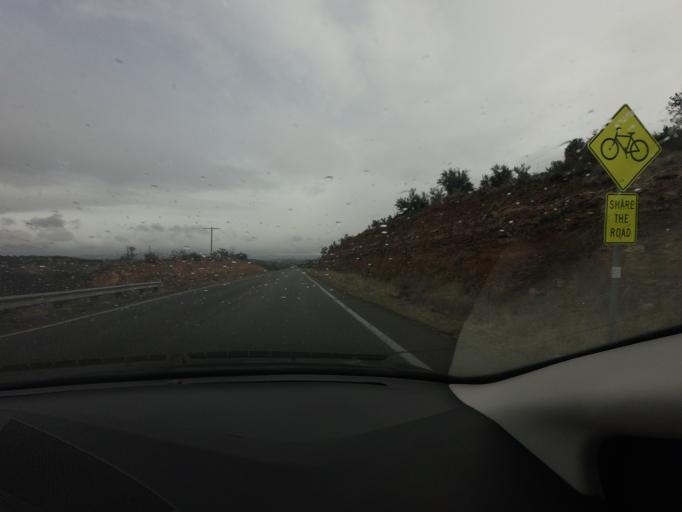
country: US
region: Arizona
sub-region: Yavapai County
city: Lake Montezuma
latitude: 34.6685
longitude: -111.8311
